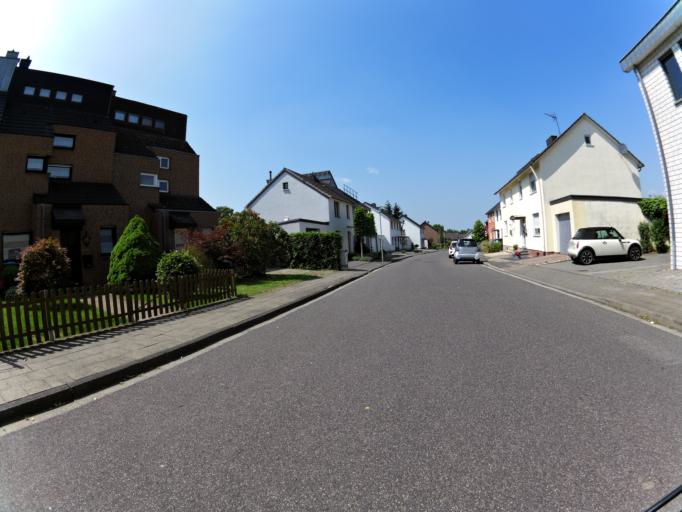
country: DE
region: North Rhine-Westphalia
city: Siersdorf
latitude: 50.8997
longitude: 6.2330
